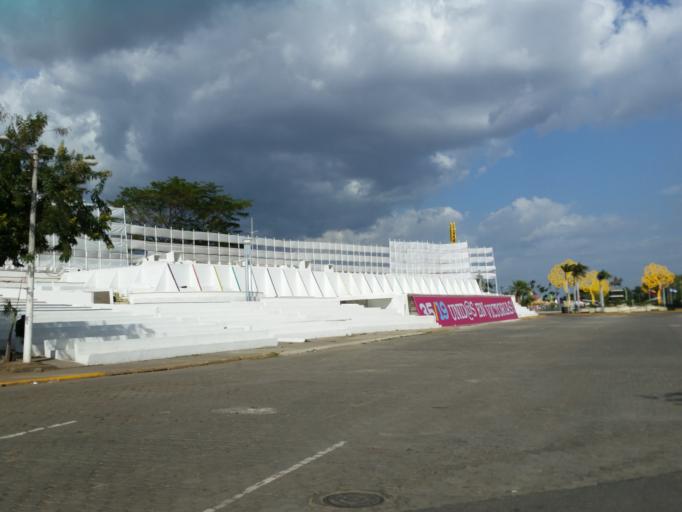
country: NI
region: Managua
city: Managua
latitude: 12.1606
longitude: -86.2745
